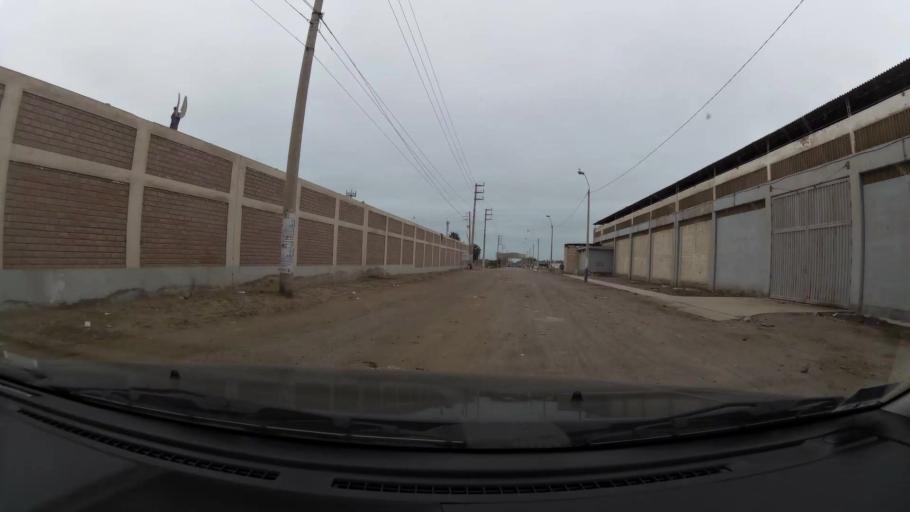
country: PE
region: Ica
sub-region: Provincia de Pisco
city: Pisco
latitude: -13.7092
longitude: -76.1968
